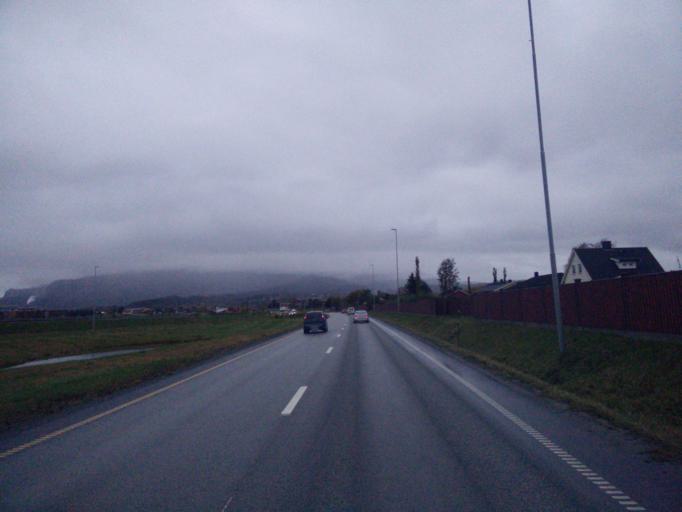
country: NO
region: Nord-Trondelag
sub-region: Stjordal
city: Stjordal
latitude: 63.4601
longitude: 10.9113
